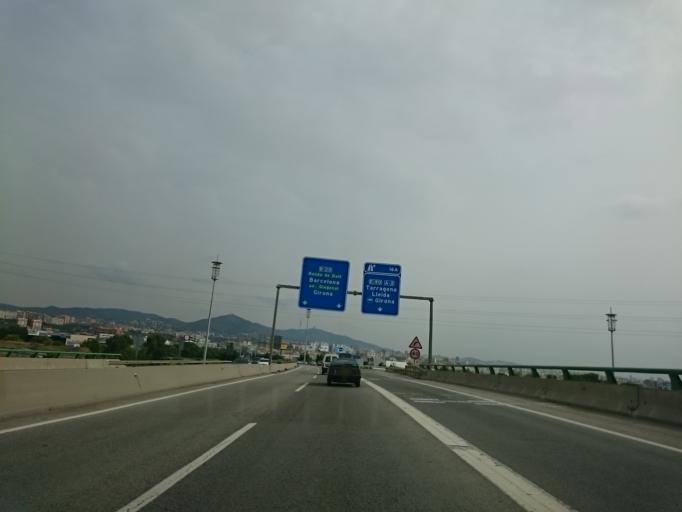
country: ES
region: Catalonia
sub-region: Provincia de Barcelona
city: Cornella de Llobregat
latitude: 41.3442
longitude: 2.0915
